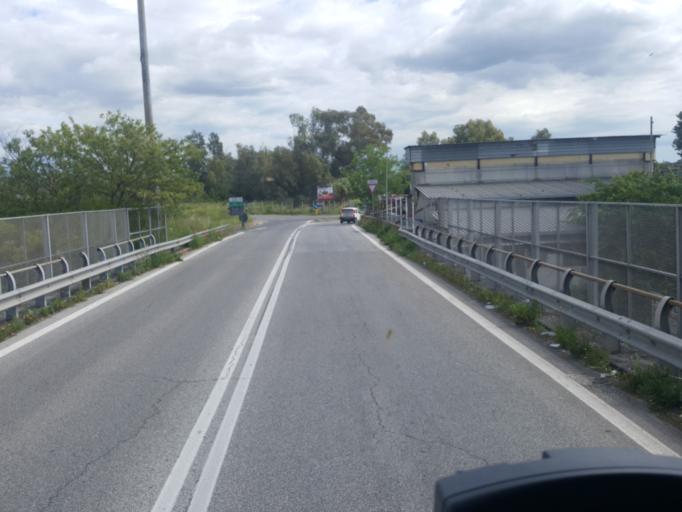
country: IT
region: Latium
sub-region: Citta metropolitana di Roma Capitale
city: La Massimina-Casal Lumbroso
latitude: 41.8873
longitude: 12.3651
